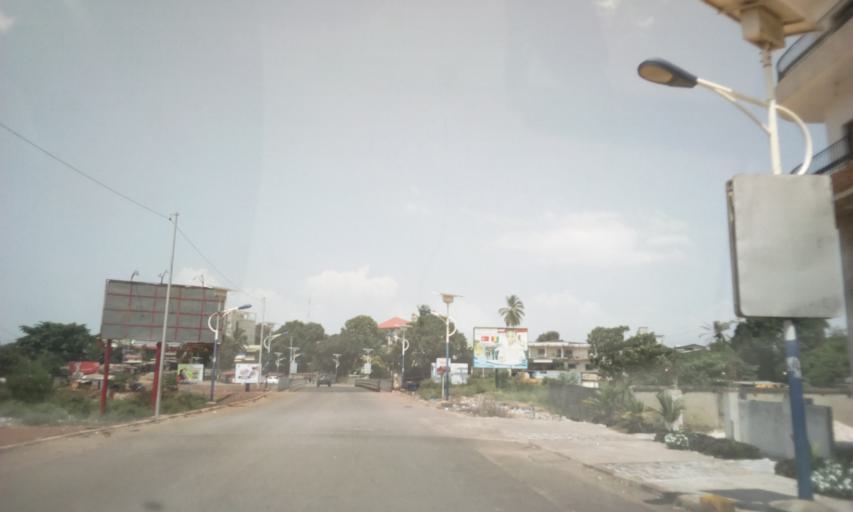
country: GN
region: Conakry
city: Conakry
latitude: 9.5721
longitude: -13.6641
